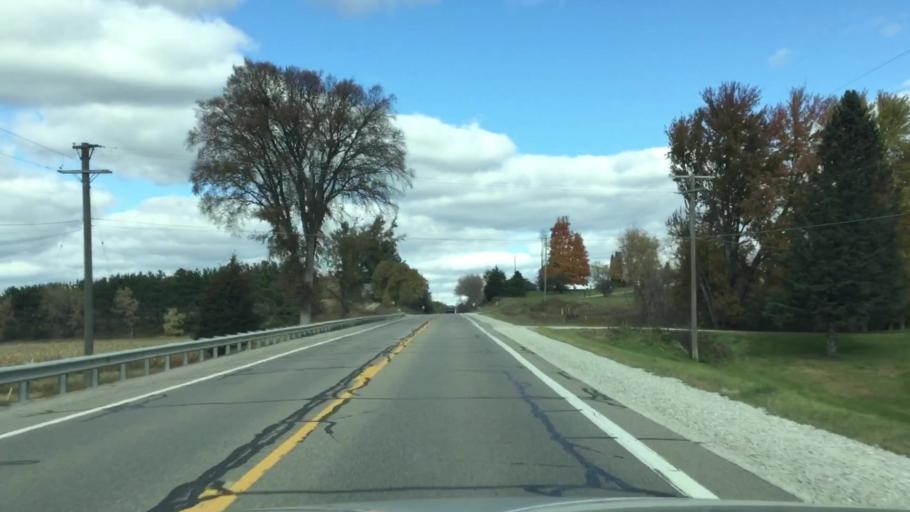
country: US
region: Michigan
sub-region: Lapeer County
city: Lapeer
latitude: 43.0976
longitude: -83.3080
